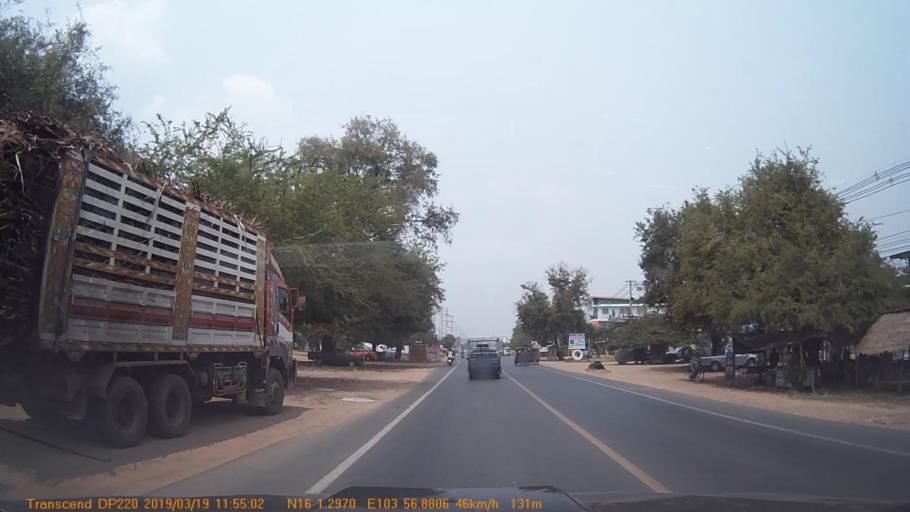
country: TH
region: Roi Et
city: Ban Selaphum
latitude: 16.0217
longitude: 103.9479
